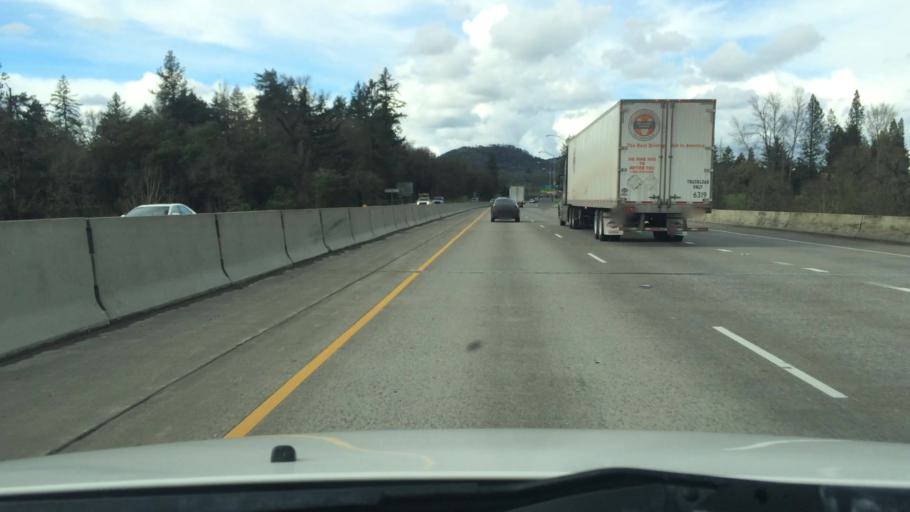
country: US
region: Oregon
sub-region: Douglas County
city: Roseburg
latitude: 43.2189
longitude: -123.3578
